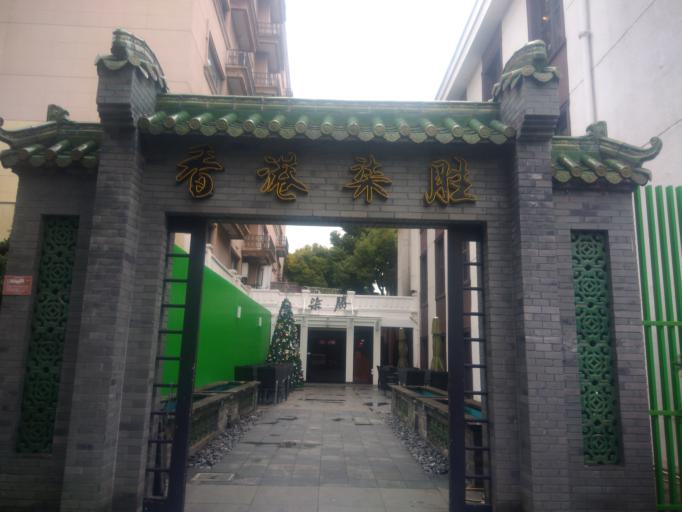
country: CN
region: Shanghai Shi
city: Changzheng
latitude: 31.1921
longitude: 121.3715
